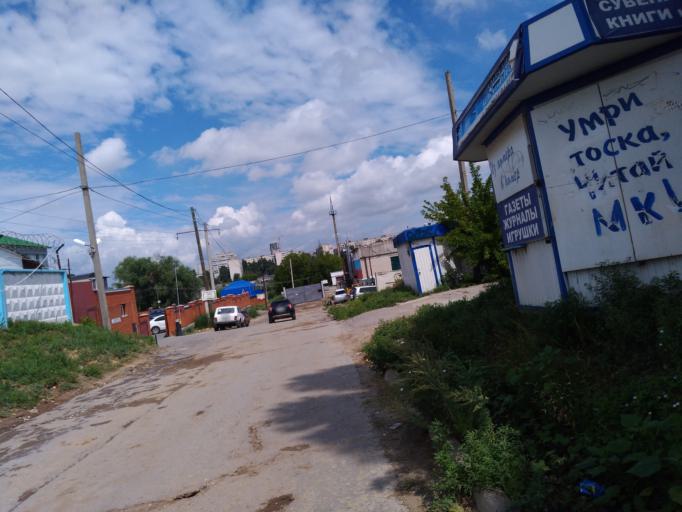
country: RU
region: Volgograd
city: Volgograd
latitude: 48.7122
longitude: 44.4621
